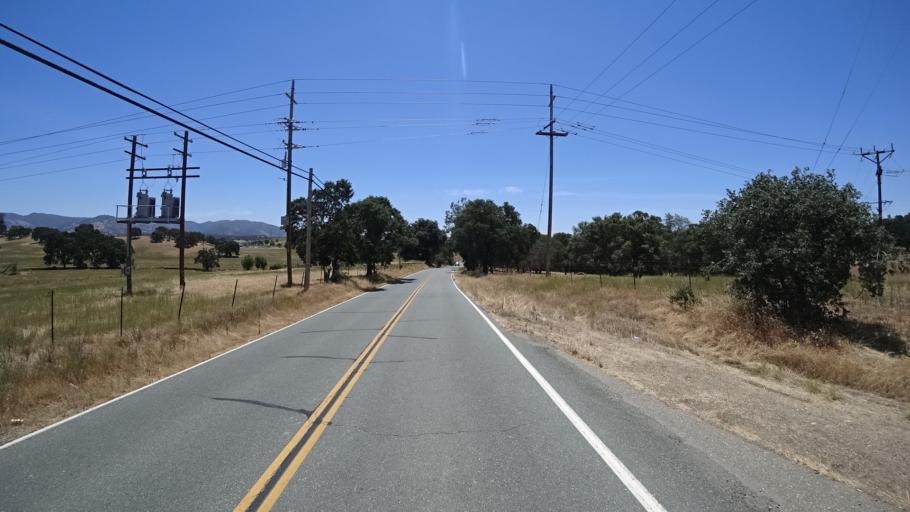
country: US
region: California
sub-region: Calaveras County
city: Valley Springs
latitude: 38.1996
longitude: -120.8268
